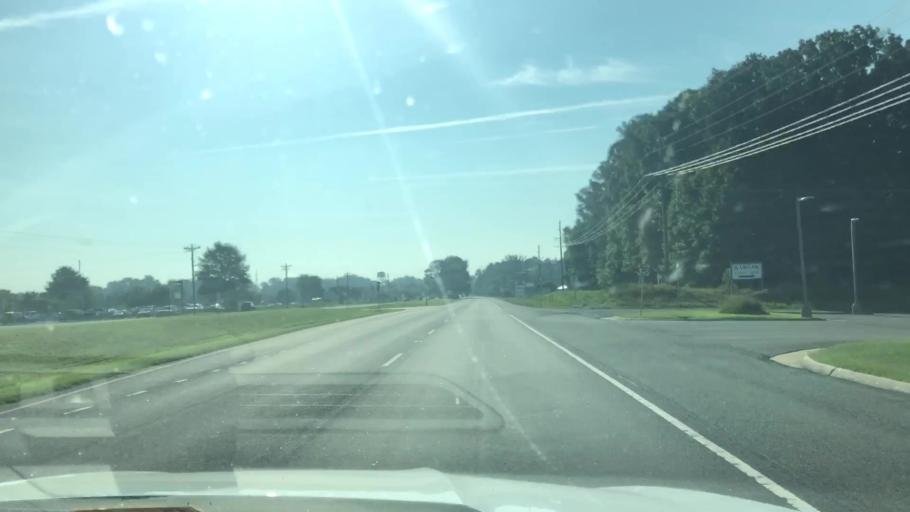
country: US
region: Virginia
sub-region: Richmond County
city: Warsaw
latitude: 37.9638
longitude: -76.7833
